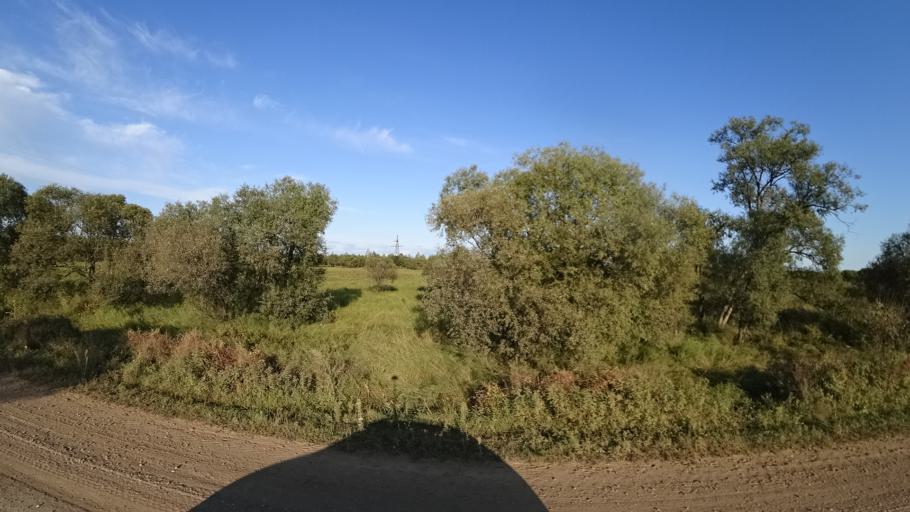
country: RU
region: Amur
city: Arkhara
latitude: 49.3646
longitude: 130.1363
